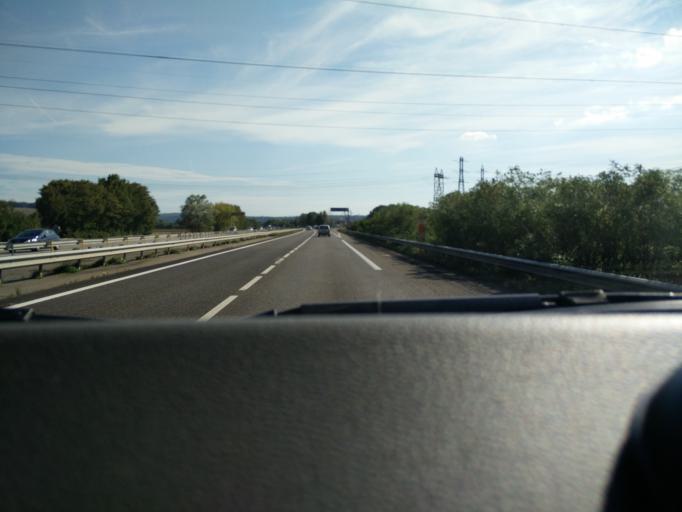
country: FR
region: Lorraine
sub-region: Departement de Meurthe-et-Moselle
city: Dieulouard
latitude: 48.8597
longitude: 6.0904
